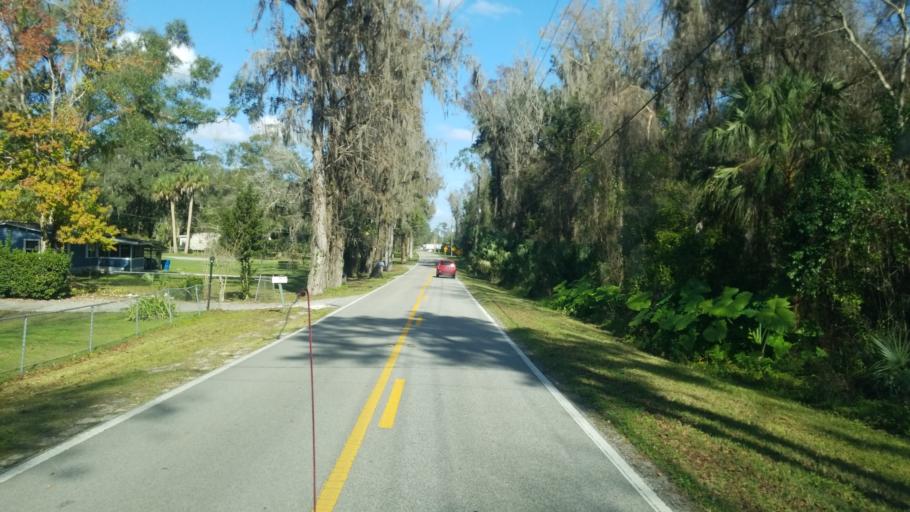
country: US
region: Florida
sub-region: Hernando County
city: Brooksville
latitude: 28.5879
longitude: -82.3751
